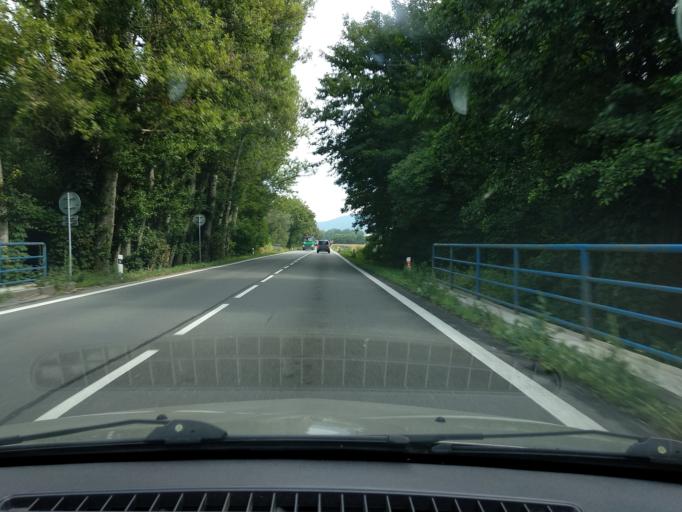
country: CZ
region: Olomoucky
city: Postrelmov
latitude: 49.9190
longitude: 16.9180
